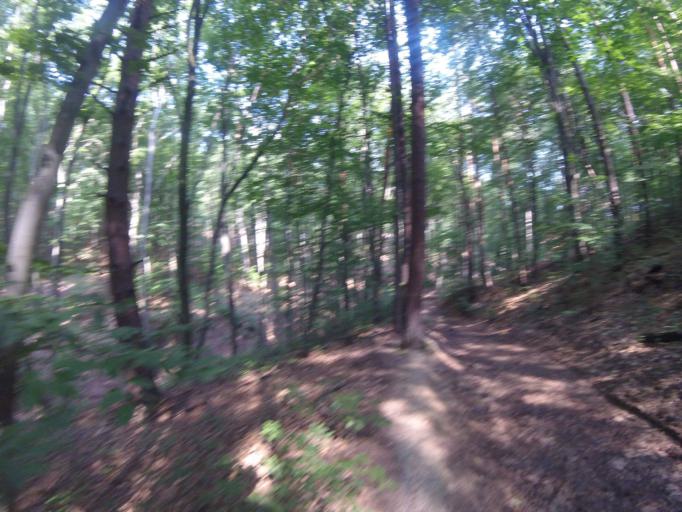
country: HU
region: Borsod-Abauj-Zemplen
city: Satoraljaujhely
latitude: 48.4487
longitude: 21.5737
